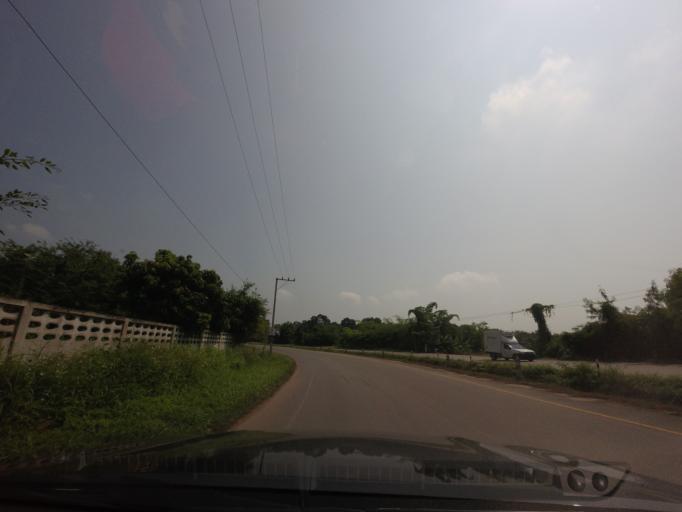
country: TH
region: Nan
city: Nan
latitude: 18.7871
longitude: 100.7468
